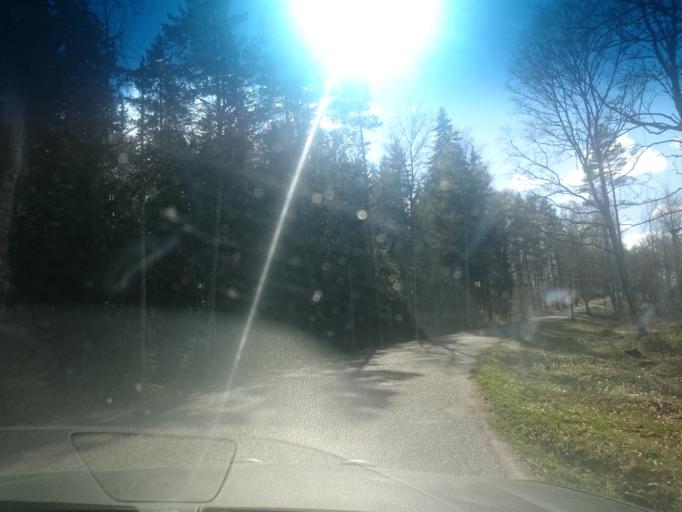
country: SE
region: Kronoberg
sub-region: Vaxjo Kommun
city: Braas
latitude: 57.1462
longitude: 15.1600
